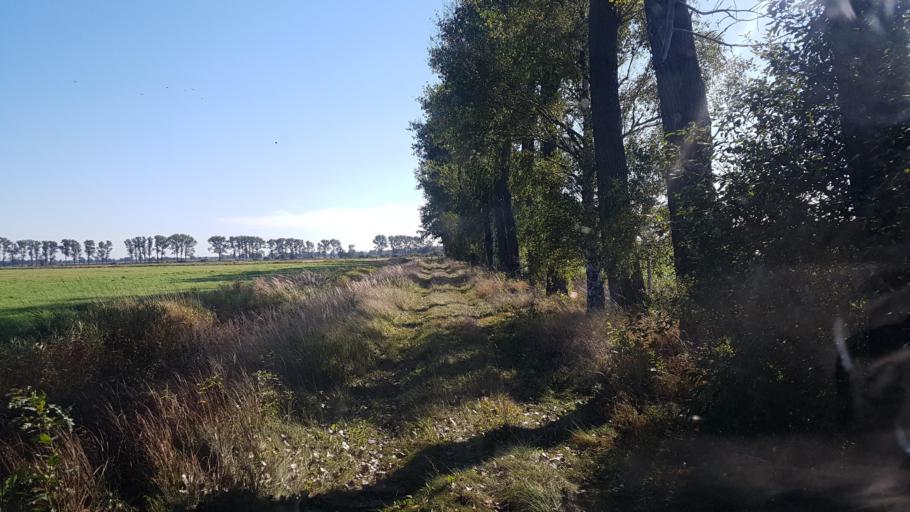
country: DE
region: Brandenburg
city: Plessa
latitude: 51.4630
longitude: 13.5750
